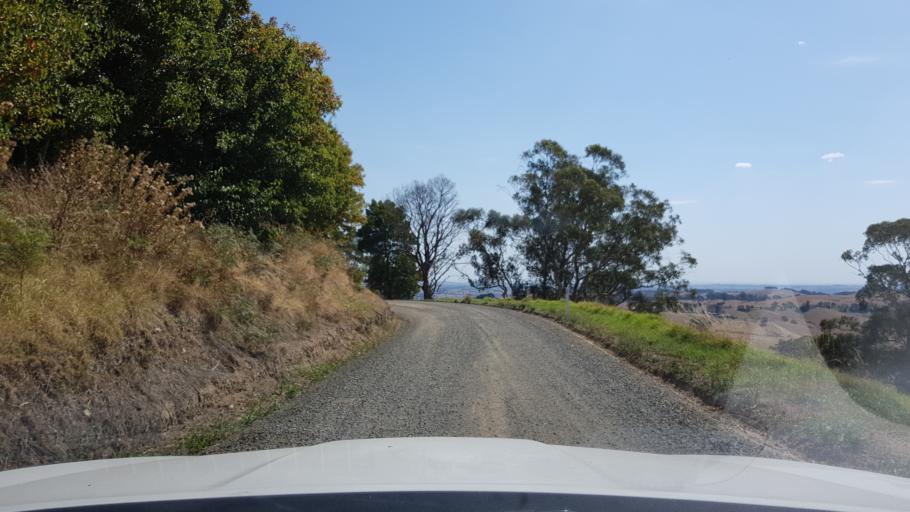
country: AU
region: Victoria
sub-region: Baw Baw
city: Warragul
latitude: -38.2863
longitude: 145.9194
